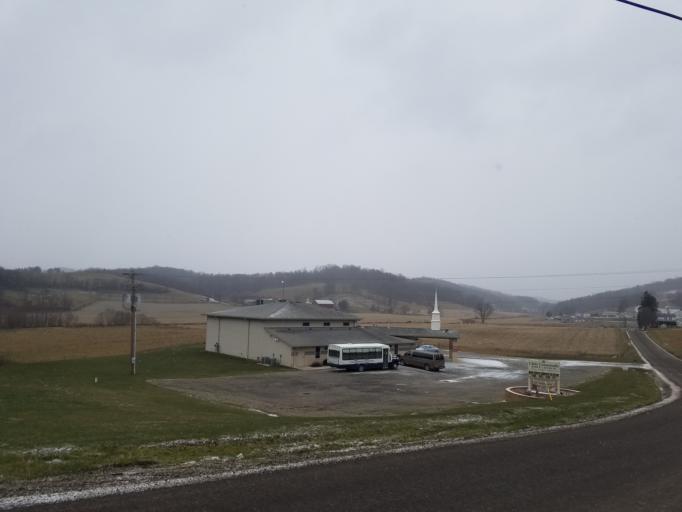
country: US
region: Ohio
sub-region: Coshocton County
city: West Lafayette
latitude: 40.3795
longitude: -81.7516
